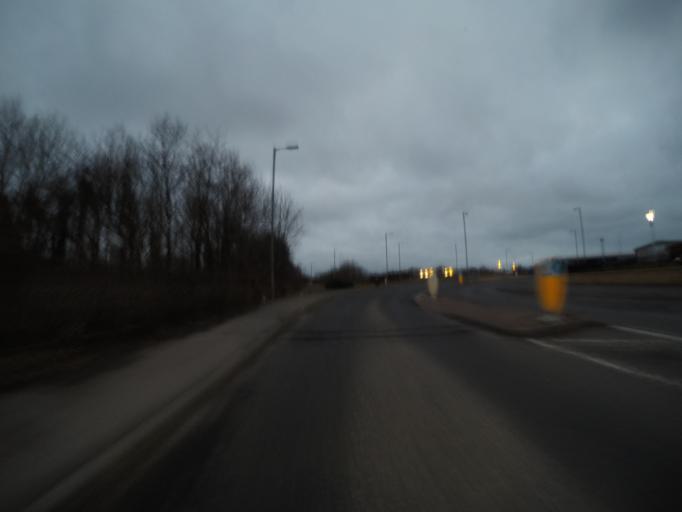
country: GB
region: Scotland
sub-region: North Ayrshire
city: Kilwinning
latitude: 55.6473
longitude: -4.6975
